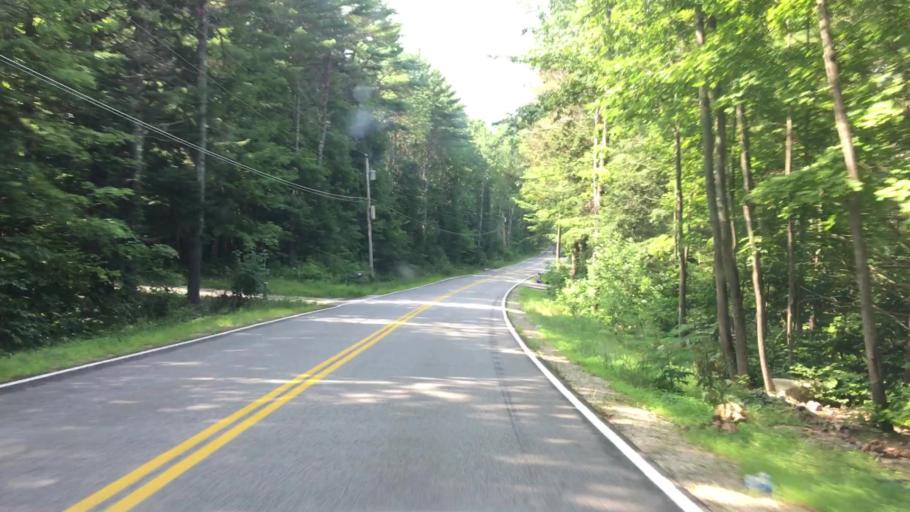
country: US
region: Maine
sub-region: Cumberland County
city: Raymond
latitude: 43.9586
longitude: -70.4186
